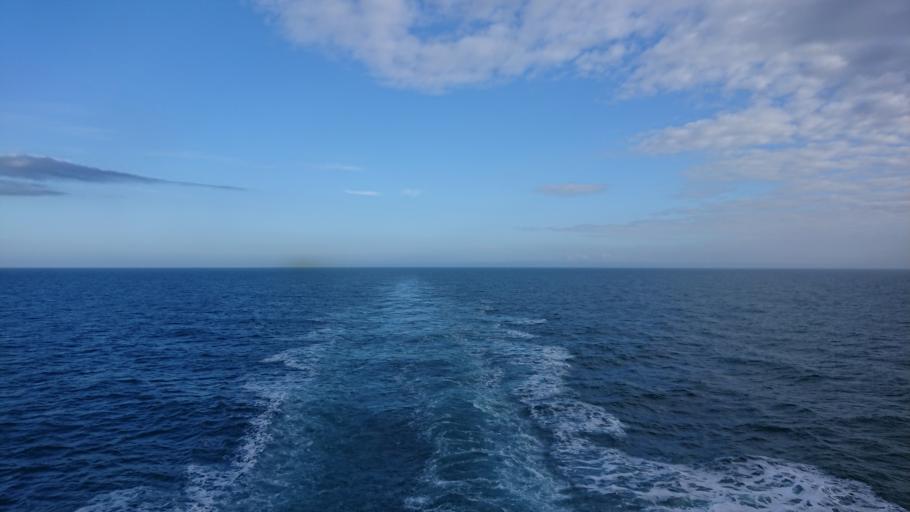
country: GB
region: Wales
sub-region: Pembrokeshire
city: Saint David's
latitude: 52.1326
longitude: -5.6054
